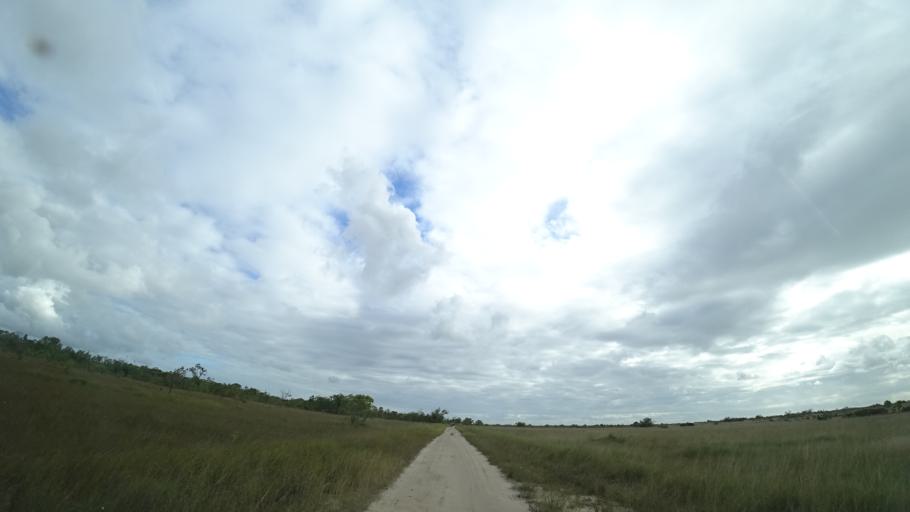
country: MZ
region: Sofala
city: Beira
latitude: -19.6152
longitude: 35.0649
